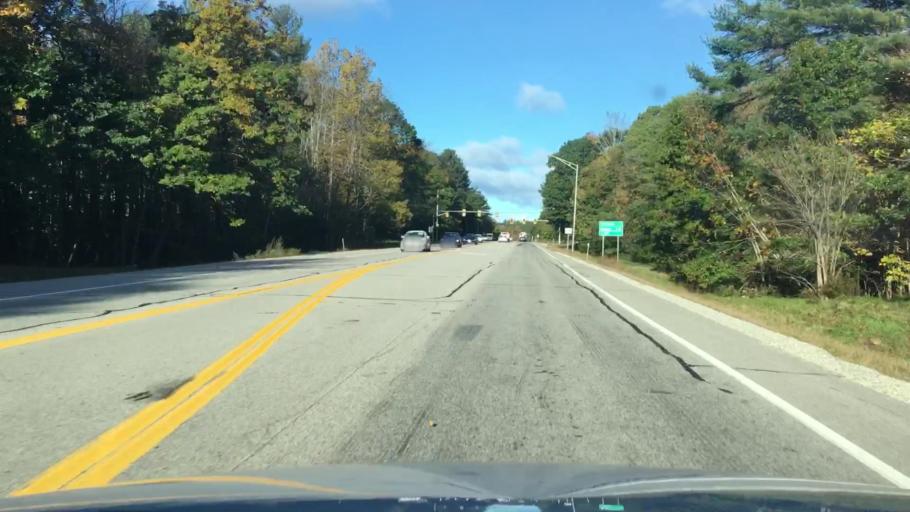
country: US
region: New Hampshire
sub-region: Strafford County
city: Madbury
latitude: 43.1523
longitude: -70.9284
